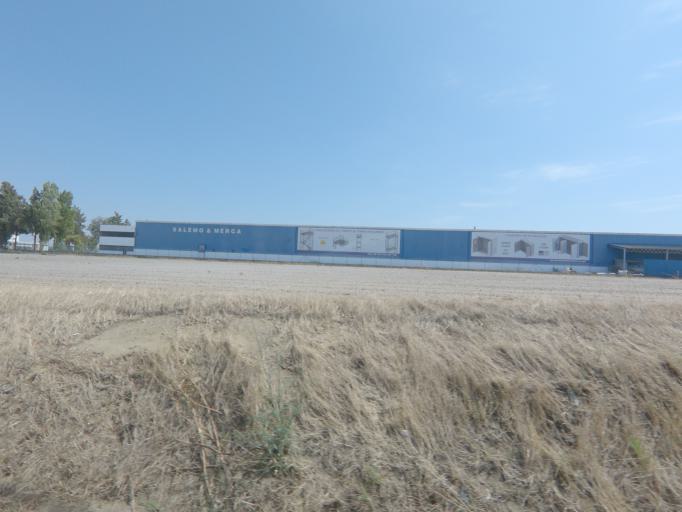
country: PT
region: Setubal
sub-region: Palmela
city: Palmela
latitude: 38.5903
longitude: -8.8482
